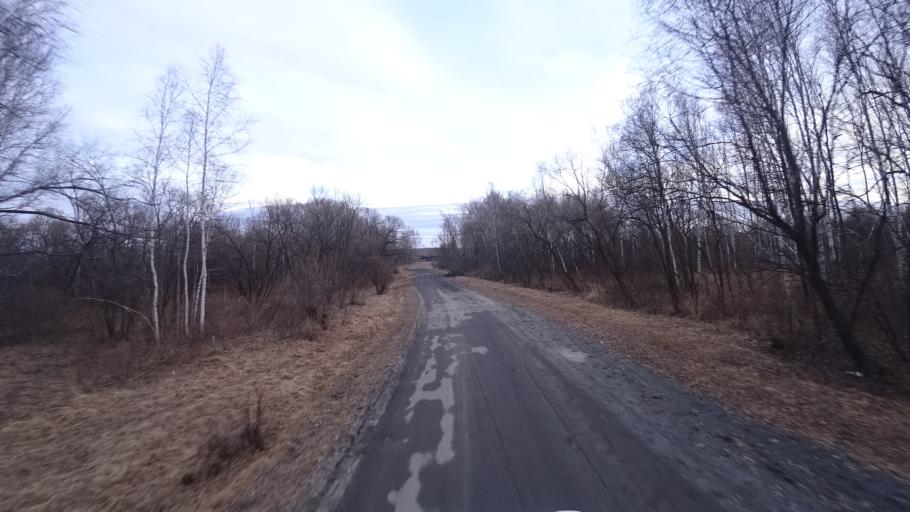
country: RU
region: Amur
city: Bureya
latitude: 50.0194
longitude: 129.7802
